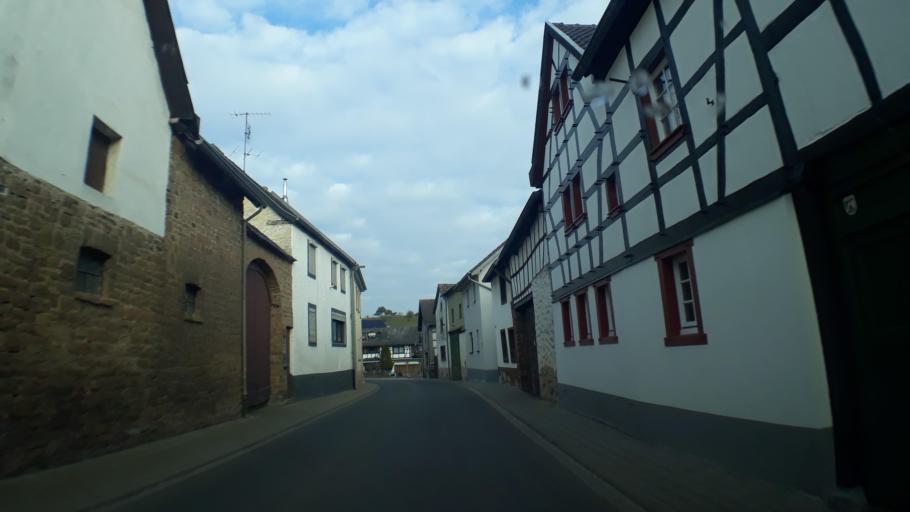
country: DE
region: North Rhine-Westphalia
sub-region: Regierungsbezirk Koln
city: Mechernich
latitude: 50.5501
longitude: 6.6862
